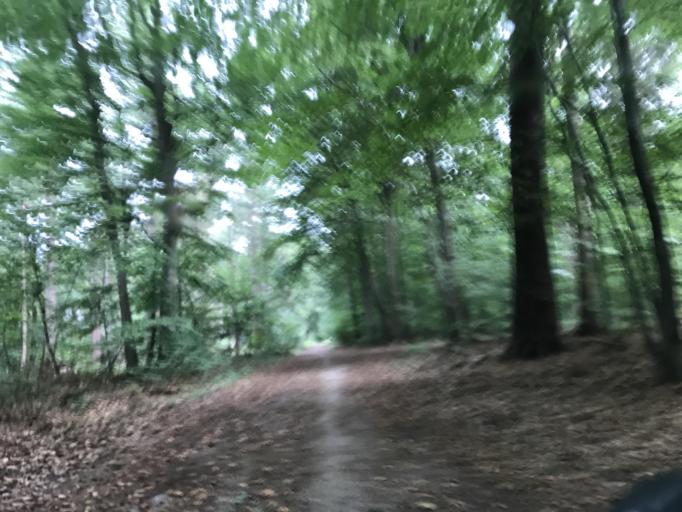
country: DE
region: Lower Saxony
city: Barendorf
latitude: 53.2166
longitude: 10.5371
